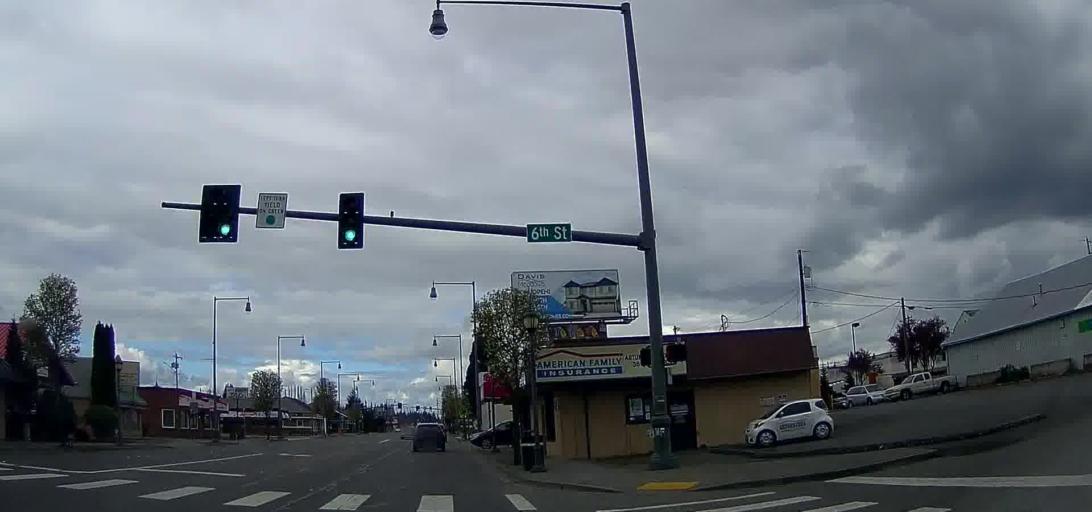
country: US
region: Washington
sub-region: Snohomish County
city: Marysville
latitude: 48.0537
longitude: -122.1769
